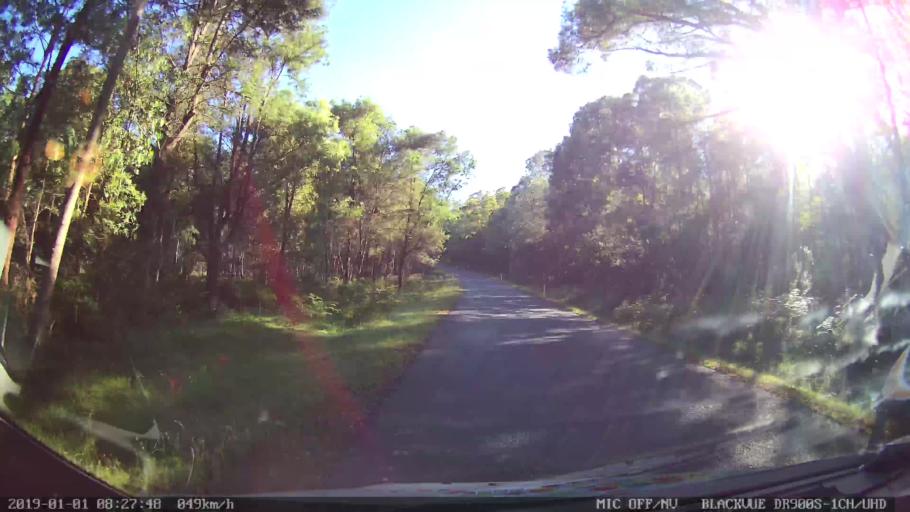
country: AU
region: New South Wales
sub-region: Snowy River
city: Jindabyne
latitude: -36.3794
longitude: 148.1859
